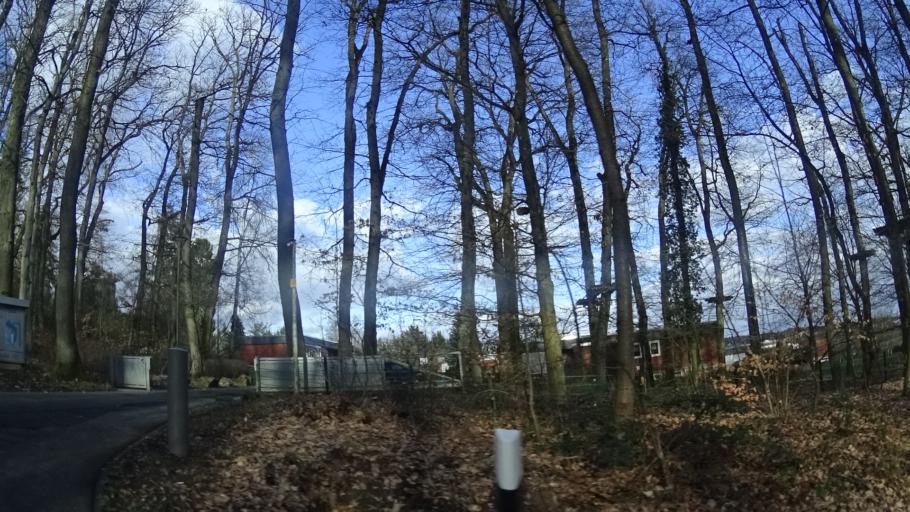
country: DE
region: Hesse
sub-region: Regierungsbezirk Darmstadt
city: Wiesbaden
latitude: 50.1045
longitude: 8.2436
